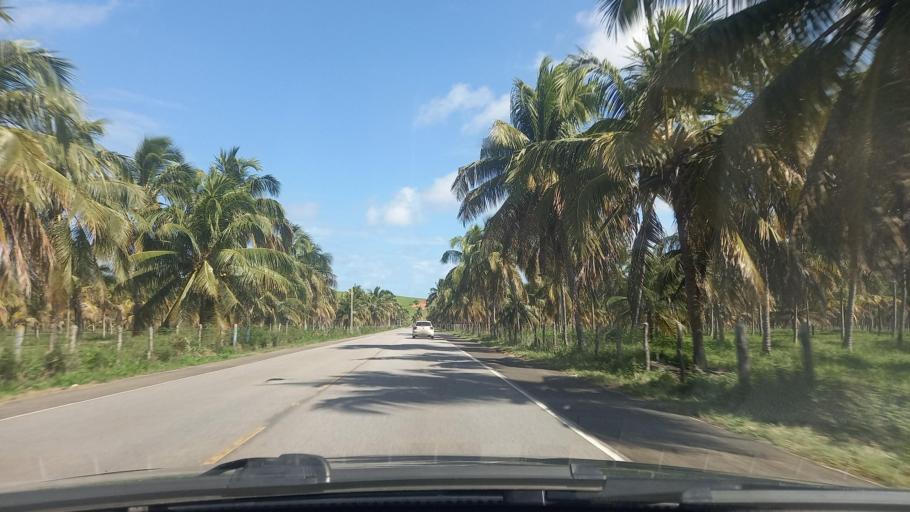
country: BR
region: Alagoas
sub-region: Marechal Deodoro
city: Marechal Deodoro
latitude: -9.8547
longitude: -35.9183
